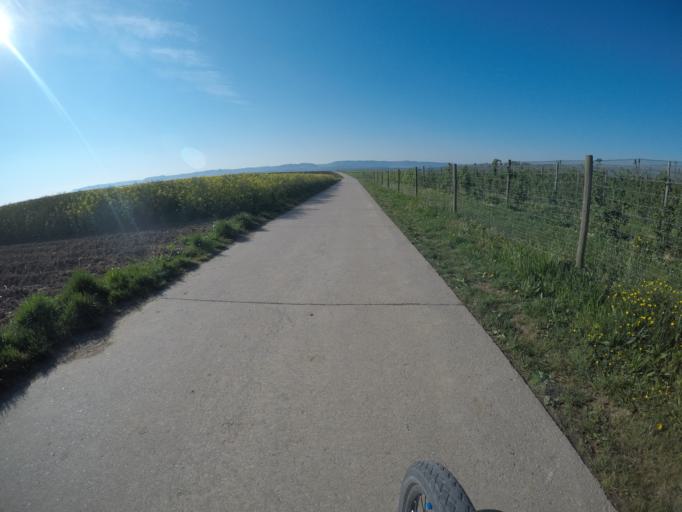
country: DE
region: Baden-Wuerttemberg
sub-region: Regierungsbezirk Stuttgart
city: Wolfschlugen
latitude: 48.6454
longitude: 9.2597
